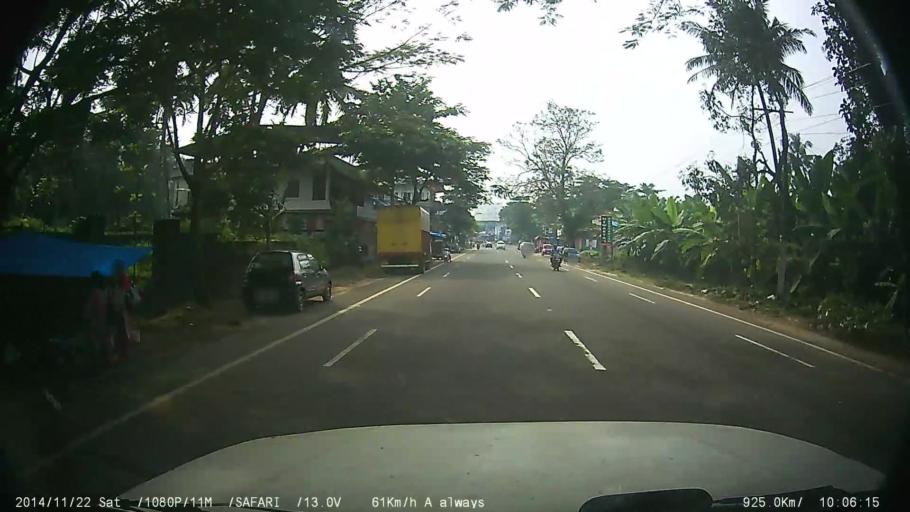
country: IN
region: Kerala
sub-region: Ernakulam
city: Muvattupula
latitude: 10.0475
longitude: 76.5328
